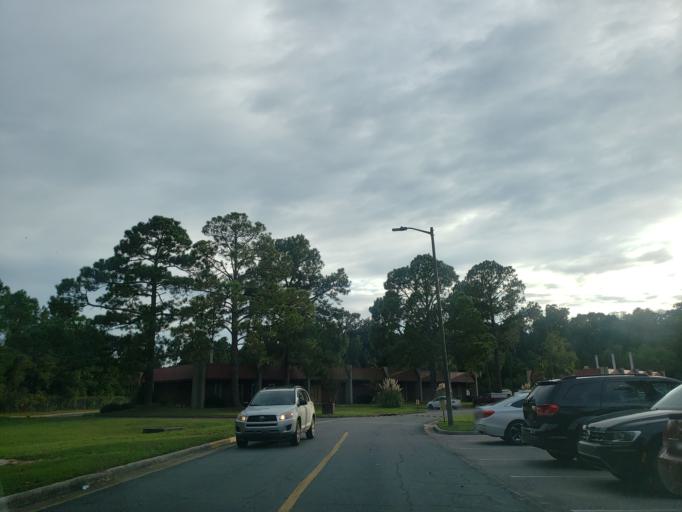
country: US
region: Georgia
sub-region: Chatham County
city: Isle of Hope
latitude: 31.9985
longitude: -81.0809
